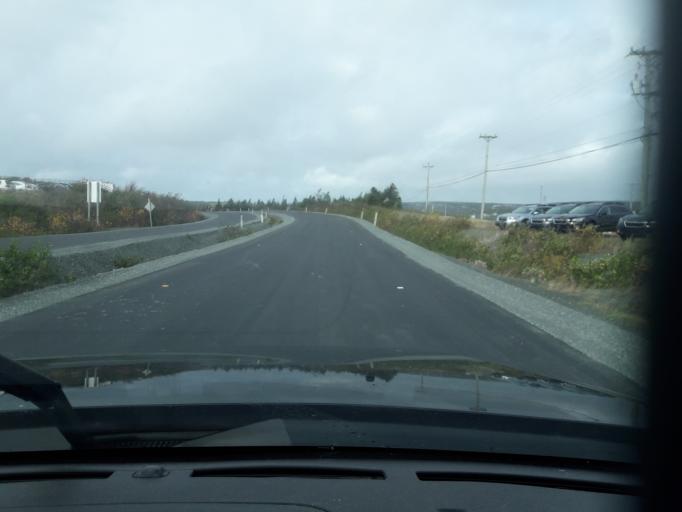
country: CA
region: Newfoundland and Labrador
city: Mount Pearl
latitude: 47.5543
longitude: -52.7708
